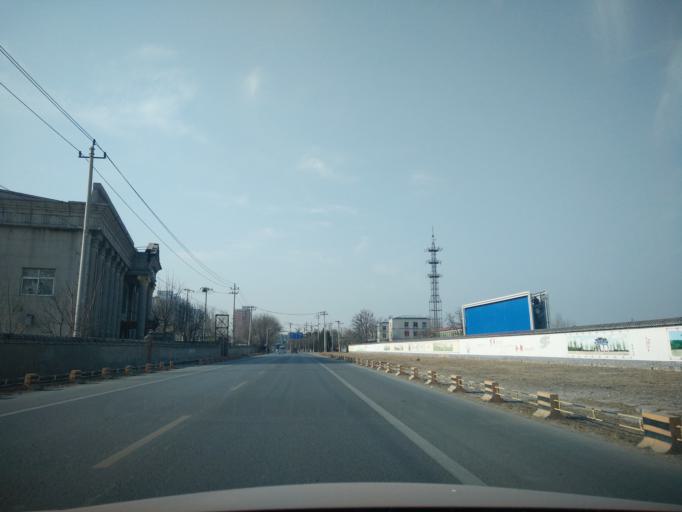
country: CN
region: Beijing
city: Yinghai
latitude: 39.7650
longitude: 116.4532
